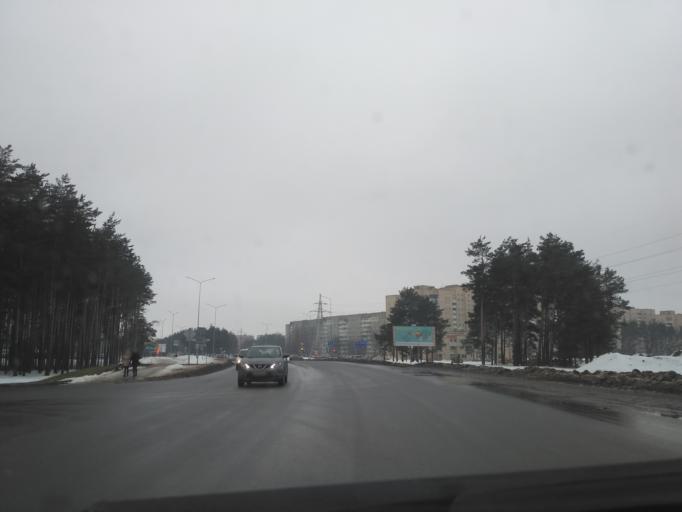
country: BY
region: Minsk
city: Horad Barysaw
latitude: 54.2018
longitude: 28.4838
